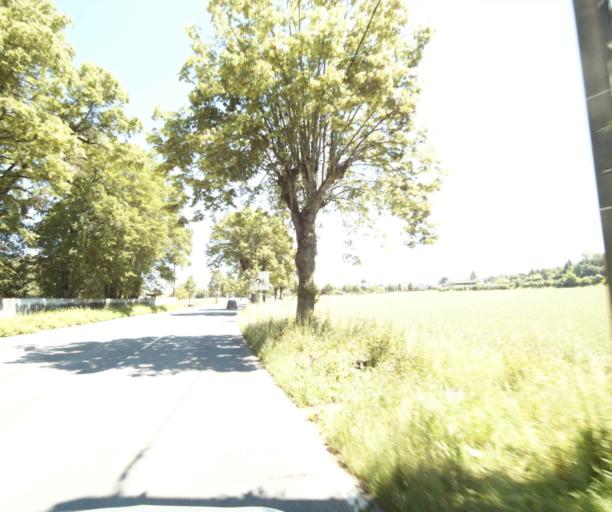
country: FR
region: Rhone-Alpes
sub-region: Departement de la Haute-Savoie
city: Anthy-sur-Leman
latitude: 46.3565
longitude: 6.4486
